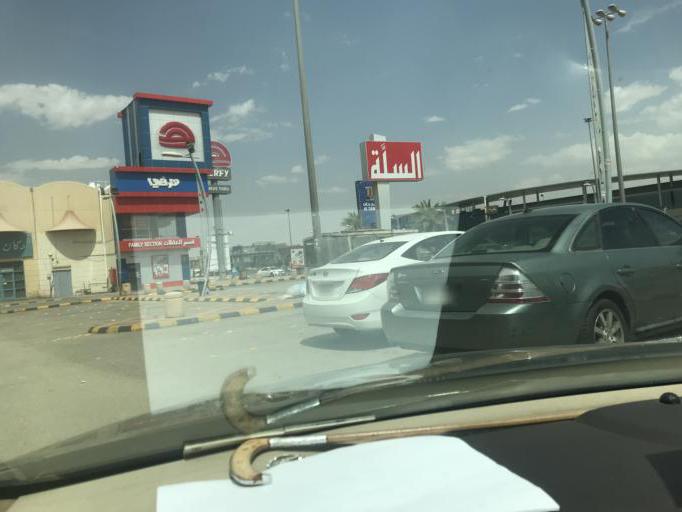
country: SA
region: Ar Riyad
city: Riyadh
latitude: 24.7287
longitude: 46.7829
